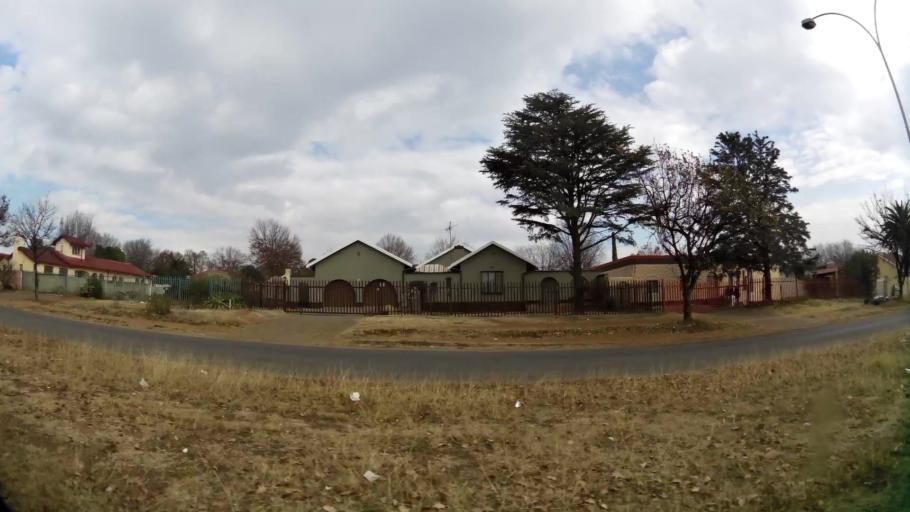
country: ZA
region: Gauteng
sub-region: Sedibeng District Municipality
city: Vanderbijlpark
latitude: -26.7148
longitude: 27.8627
